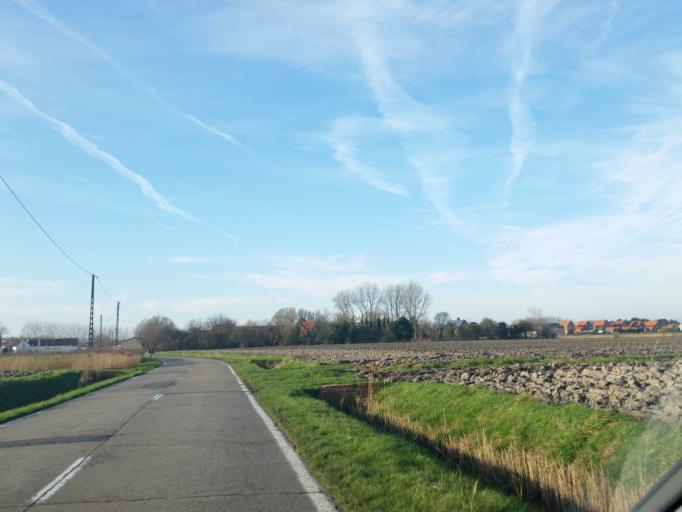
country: BE
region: Flanders
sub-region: Provincie West-Vlaanderen
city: De Haan
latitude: 51.2512
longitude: 3.0159
